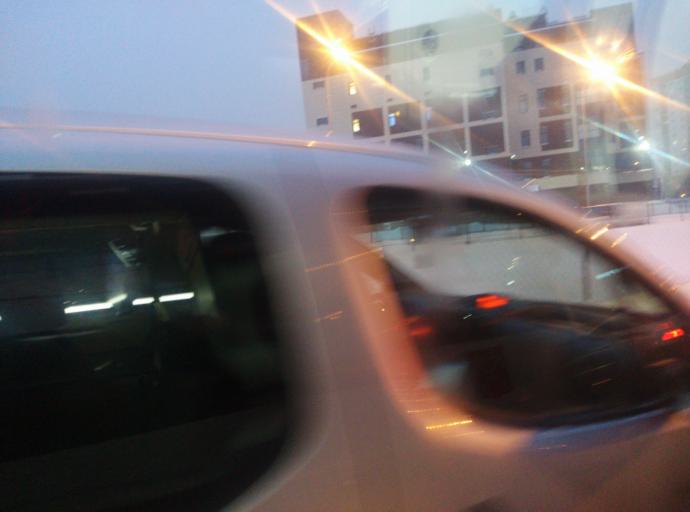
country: RU
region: St.-Petersburg
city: Kolomyagi
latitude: 60.0237
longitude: 30.2724
